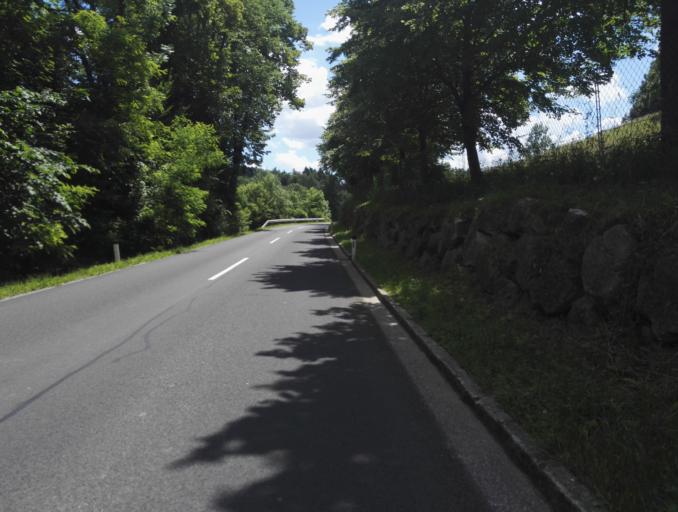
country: AT
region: Styria
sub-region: Politischer Bezirk Graz-Umgebung
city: Gratwein
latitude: 47.0891
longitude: 15.3121
